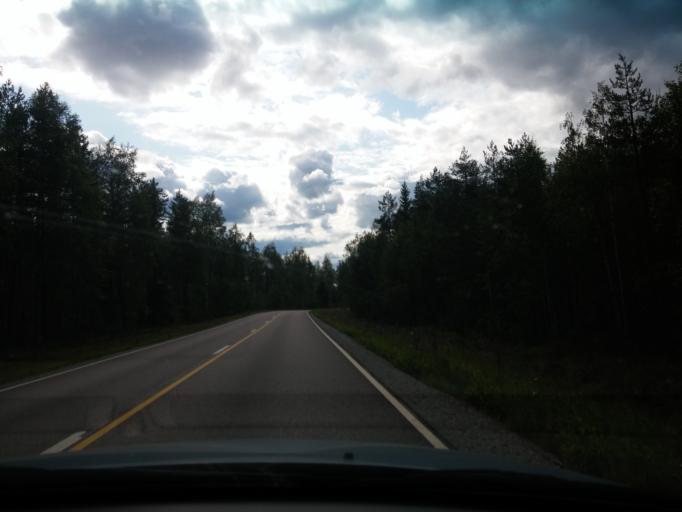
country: FI
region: Central Finland
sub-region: Saarijaervi-Viitasaari
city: Pylkoenmaeki
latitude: 62.6202
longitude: 24.7705
